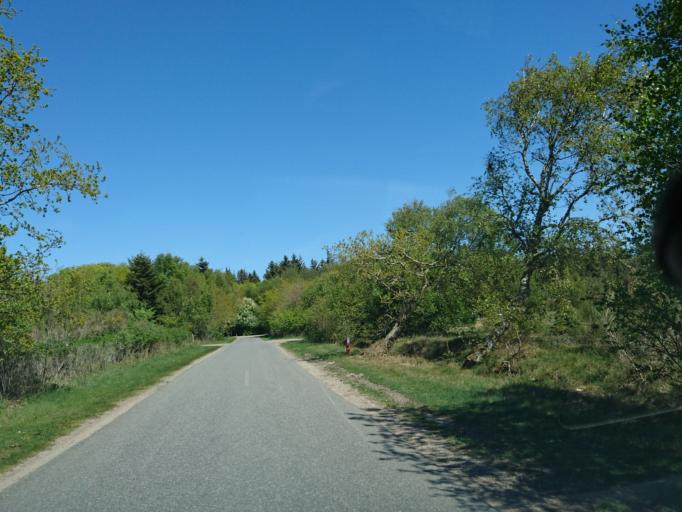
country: DK
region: North Denmark
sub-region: Hjorring Kommune
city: Sindal
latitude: 57.6019
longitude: 10.2352
